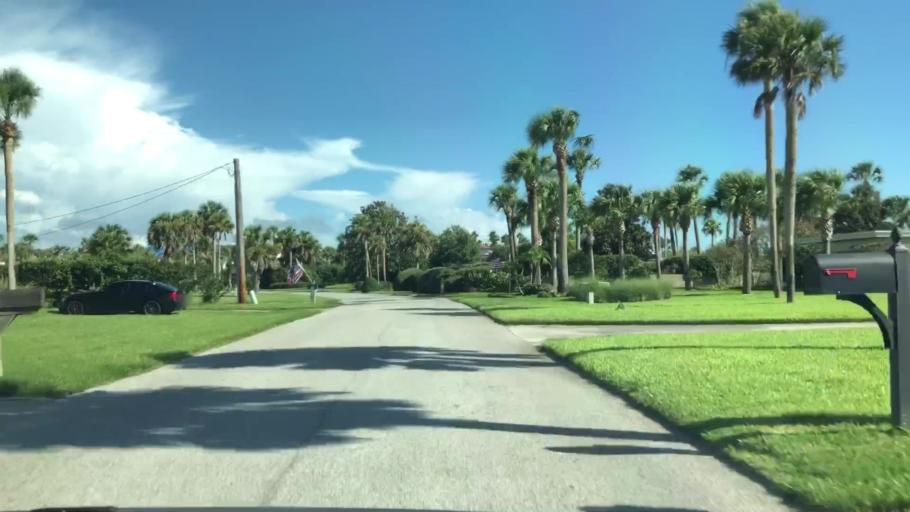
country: US
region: Florida
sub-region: Saint Johns County
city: Ponte Vedra Beach
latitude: 30.2411
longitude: -81.3816
